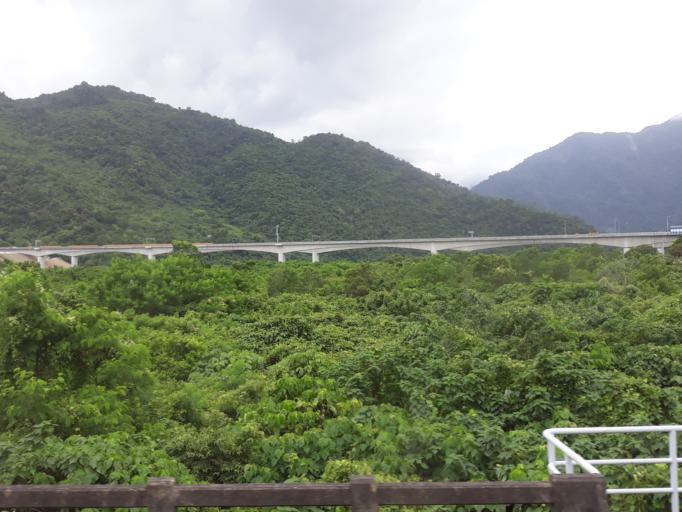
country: TW
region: Taiwan
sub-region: Yilan
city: Yilan
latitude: 24.4431
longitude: 121.7787
